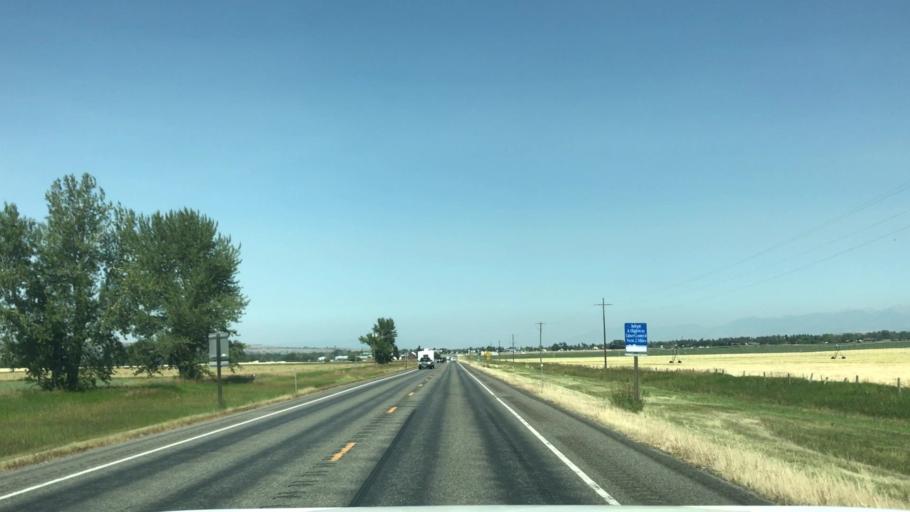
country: US
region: Montana
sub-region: Gallatin County
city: Four Corners
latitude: 45.5708
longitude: -111.1969
